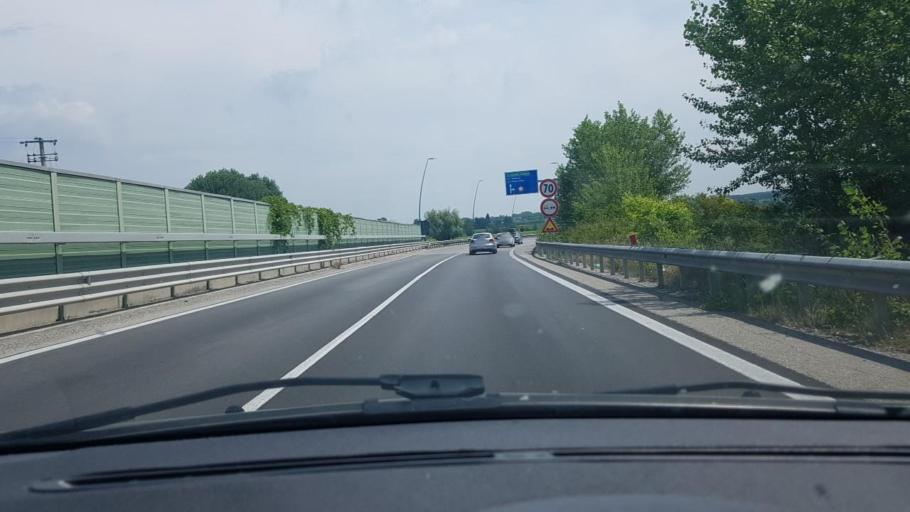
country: IT
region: Lombardy
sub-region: Provincia di Brescia
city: Pozzolengo
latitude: 45.4439
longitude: 10.6429
